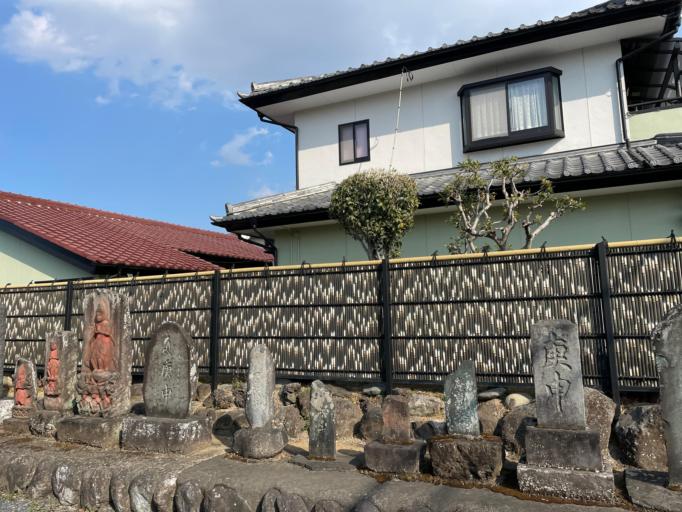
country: JP
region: Saitama
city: Yorii
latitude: 36.1254
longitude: 139.2300
